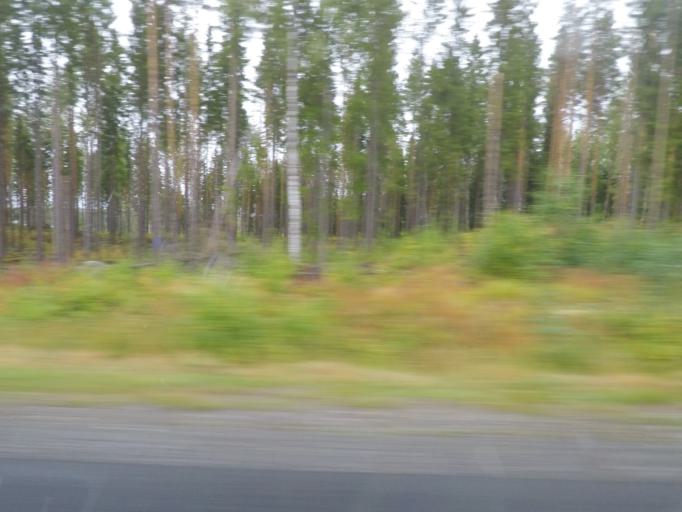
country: FI
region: Northern Savo
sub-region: Varkaus
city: Leppaevirta
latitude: 62.5050
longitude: 27.7198
